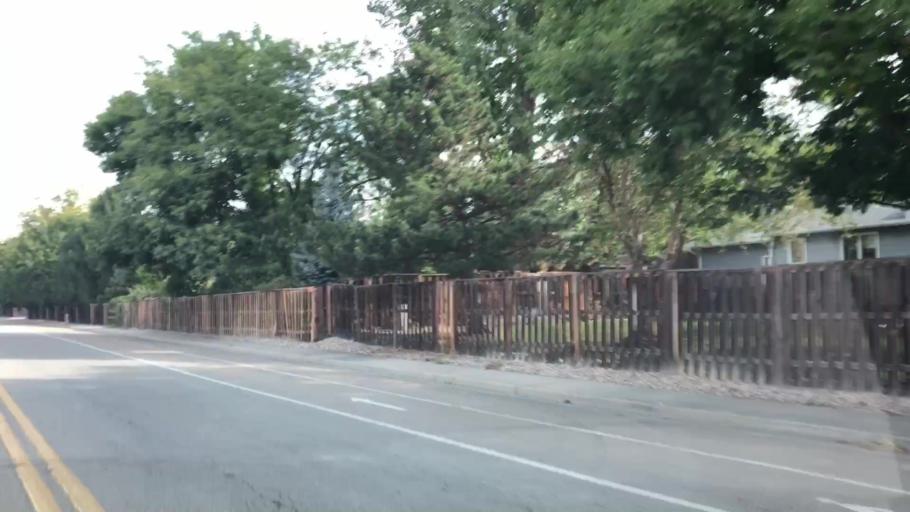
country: US
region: Colorado
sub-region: Larimer County
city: Loveland
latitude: 40.4158
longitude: -105.0536
